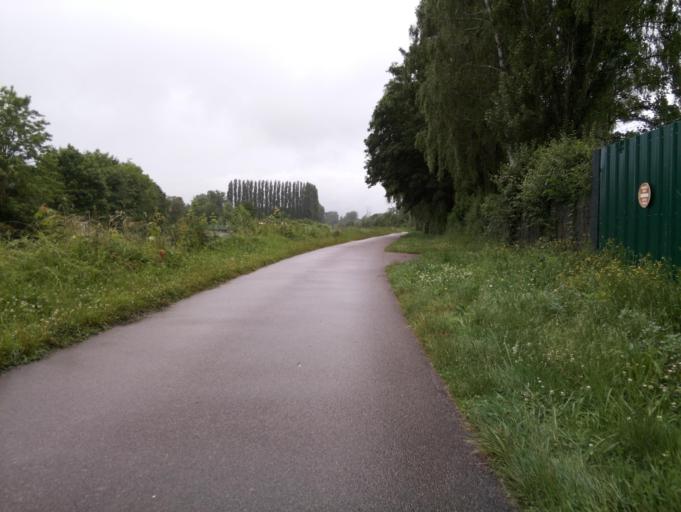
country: FR
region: Picardie
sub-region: Departement de la Somme
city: Ailly-sur-Somme
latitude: 49.9282
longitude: 2.2053
